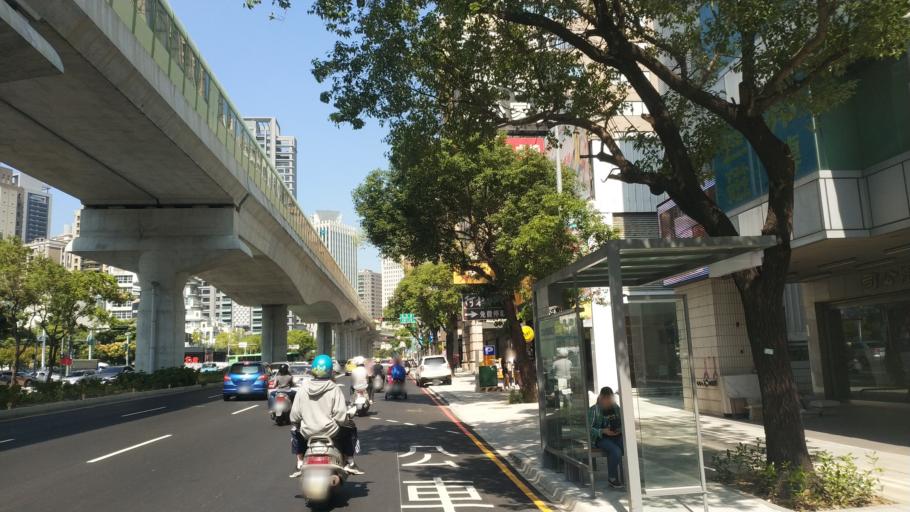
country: TW
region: Taiwan
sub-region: Taichung City
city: Taichung
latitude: 24.1546
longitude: 120.6469
